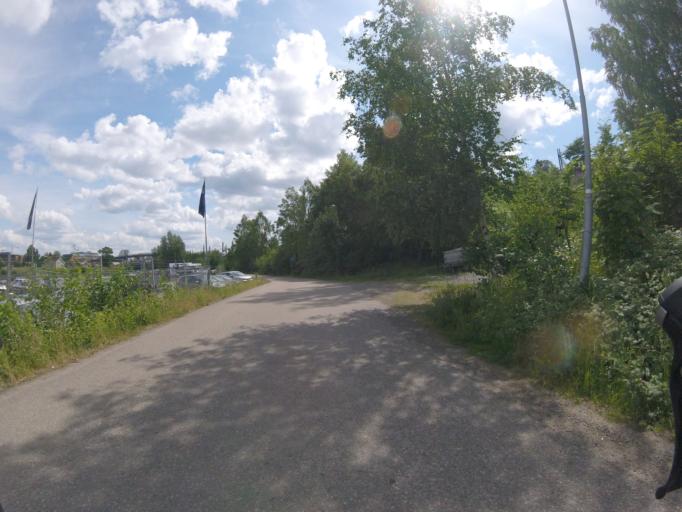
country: NO
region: Akershus
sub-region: Skedsmo
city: Lillestrom
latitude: 59.9529
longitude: 11.0322
